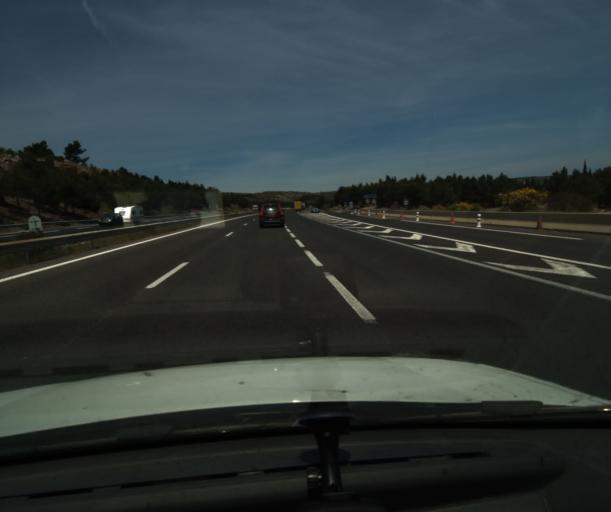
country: FR
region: Languedoc-Roussillon
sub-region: Departement des Pyrenees-Orientales
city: Salses-le-Chateau
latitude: 42.8379
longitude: 2.9104
